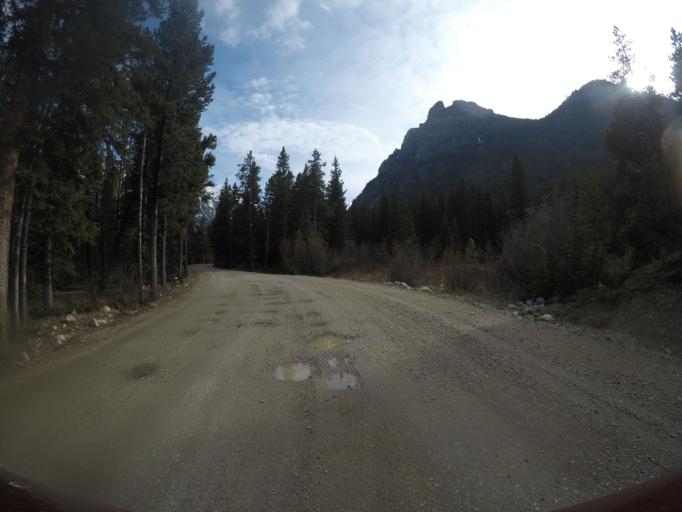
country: US
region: Montana
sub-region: Carbon County
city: Red Lodge
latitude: 45.0430
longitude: -109.4270
